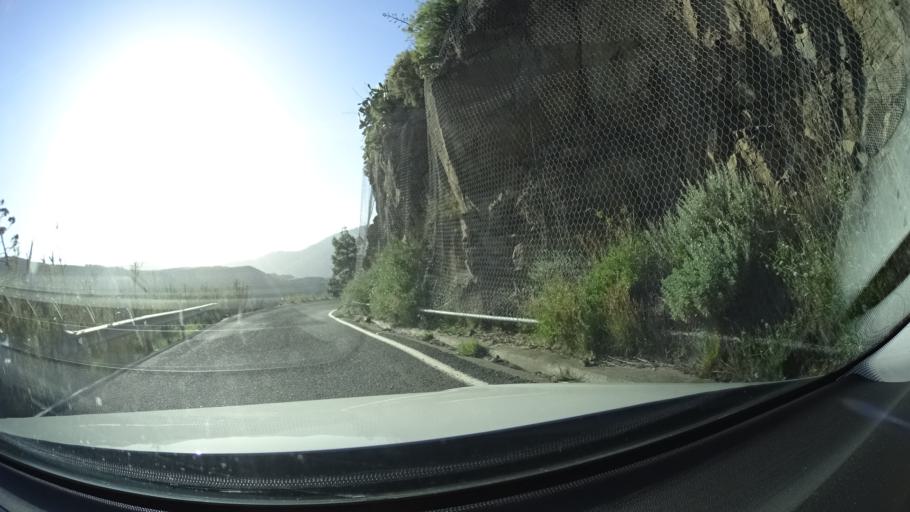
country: ES
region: Canary Islands
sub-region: Provincia de Las Palmas
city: Artenara
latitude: 28.0421
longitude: -15.6469
